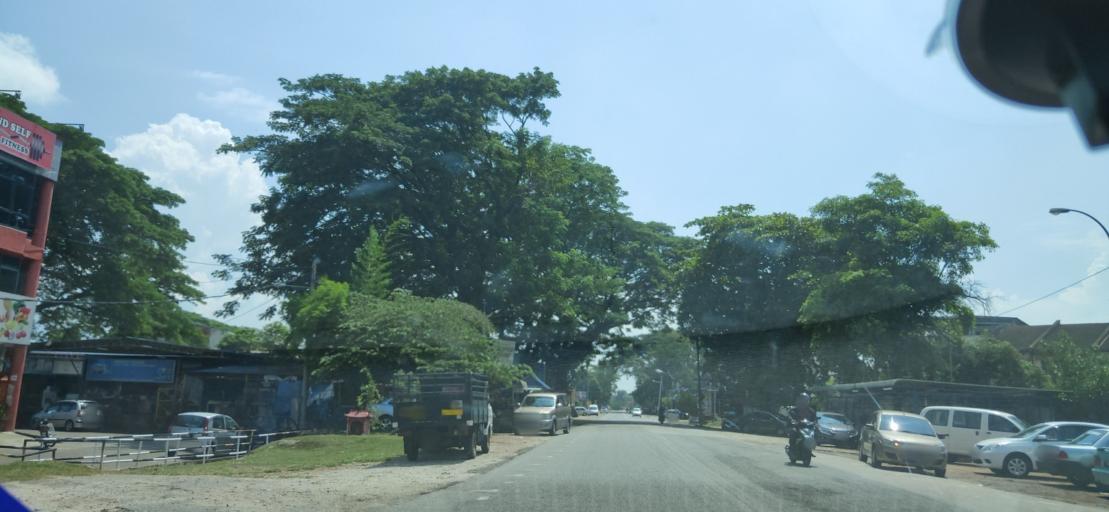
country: MY
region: Kedah
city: Sungai Petani
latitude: 5.6407
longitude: 100.4940
